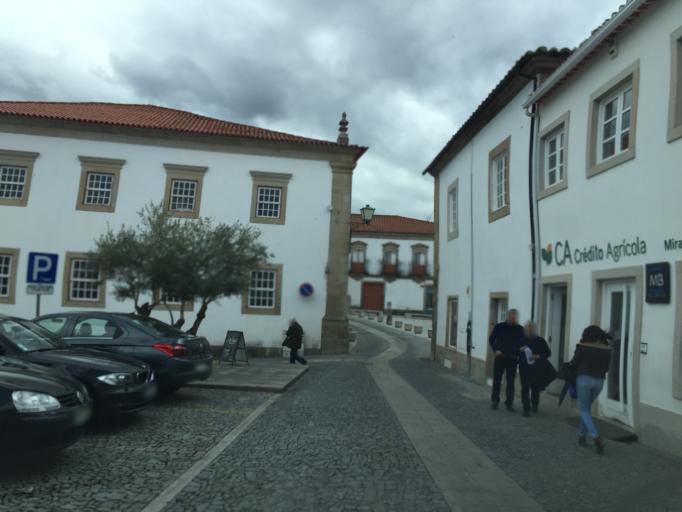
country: PT
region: Braganca
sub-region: Miranda do Douro
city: Miranda do Douro
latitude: 41.4946
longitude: -6.2738
